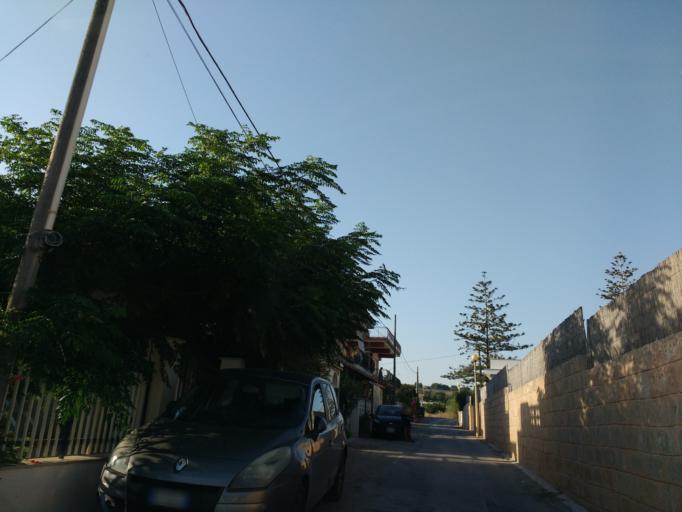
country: IT
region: Sicily
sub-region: Ragusa
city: Donnalucata
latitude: 36.7594
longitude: 14.6439
